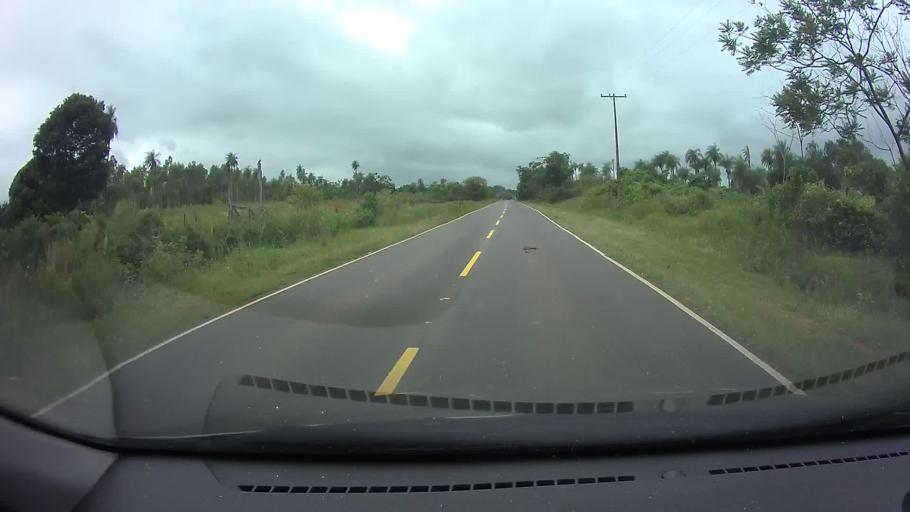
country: PY
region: Paraguari
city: Yaguaron
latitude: -25.7164
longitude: -57.3341
